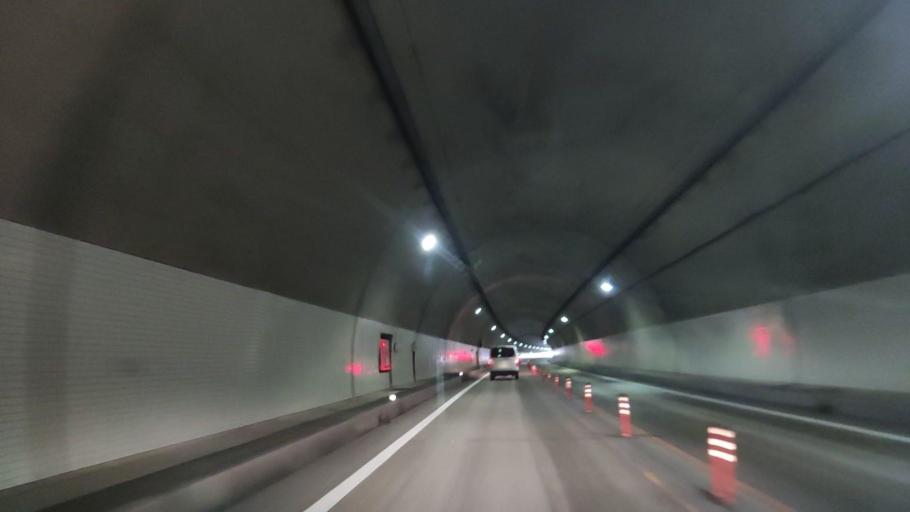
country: JP
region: Akita
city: Odate
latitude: 40.3317
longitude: 140.6098
